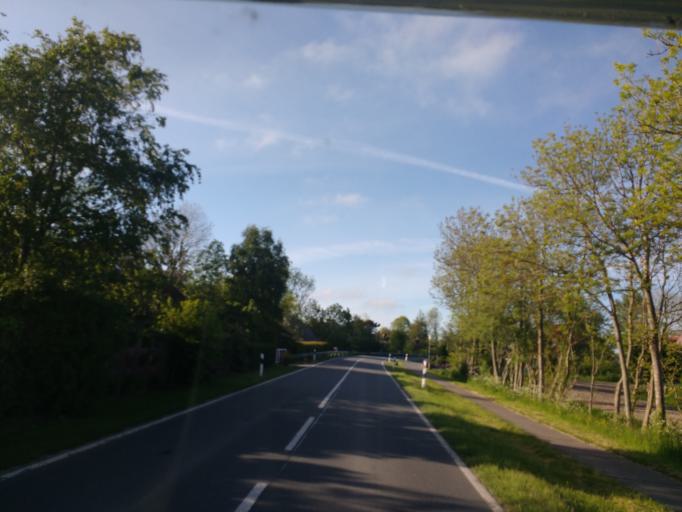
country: DE
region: Lower Saxony
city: Schillig
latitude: 53.6823
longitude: 7.9877
